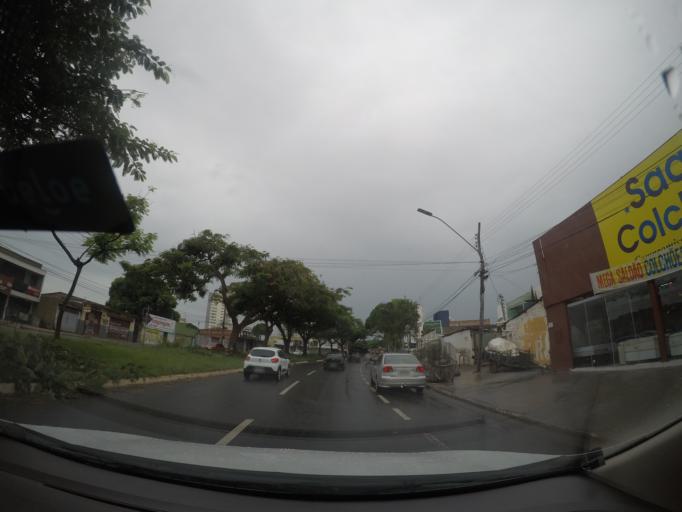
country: BR
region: Goias
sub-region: Goiania
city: Goiania
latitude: -16.7105
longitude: -49.2512
